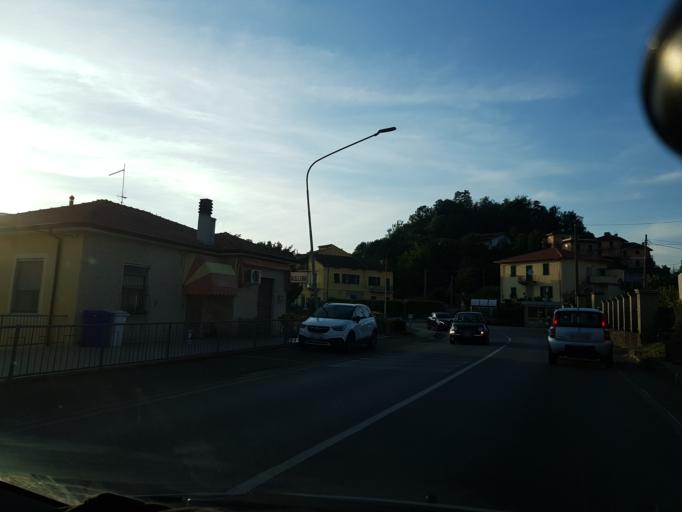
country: IT
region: Tuscany
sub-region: Provincia di Massa-Carrara
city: Aulla
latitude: 44.2061
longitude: 9.9796
